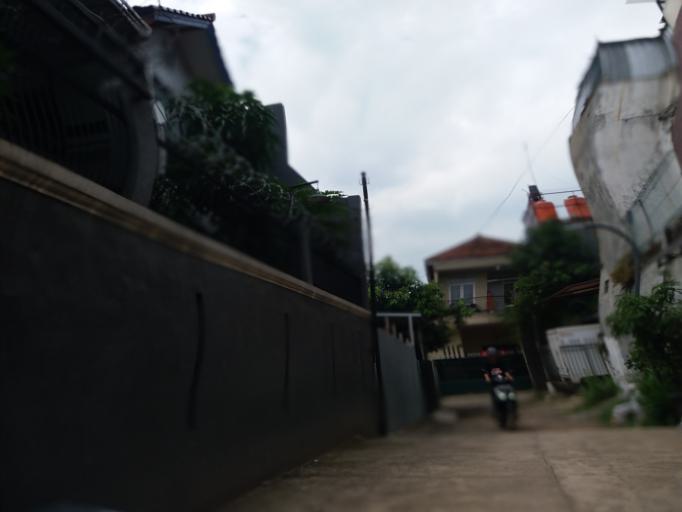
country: ID
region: West Java
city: Bandung
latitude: -6.9255
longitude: 107.6517
